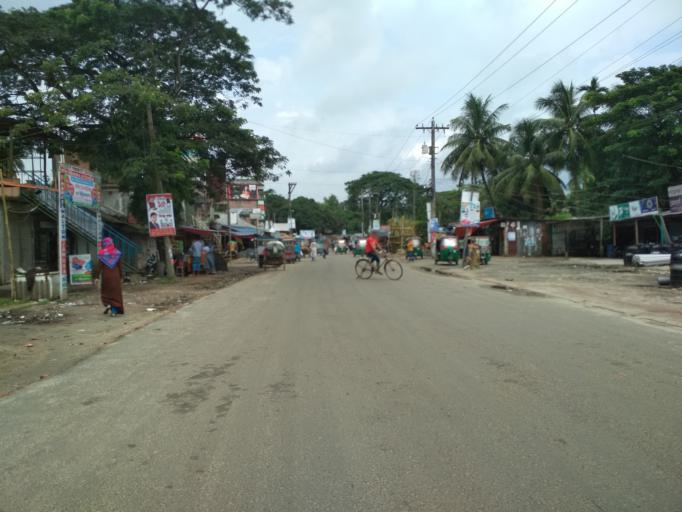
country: BD
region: Chittagong
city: Lakshmipur
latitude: 22.9692
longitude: 90.8067
